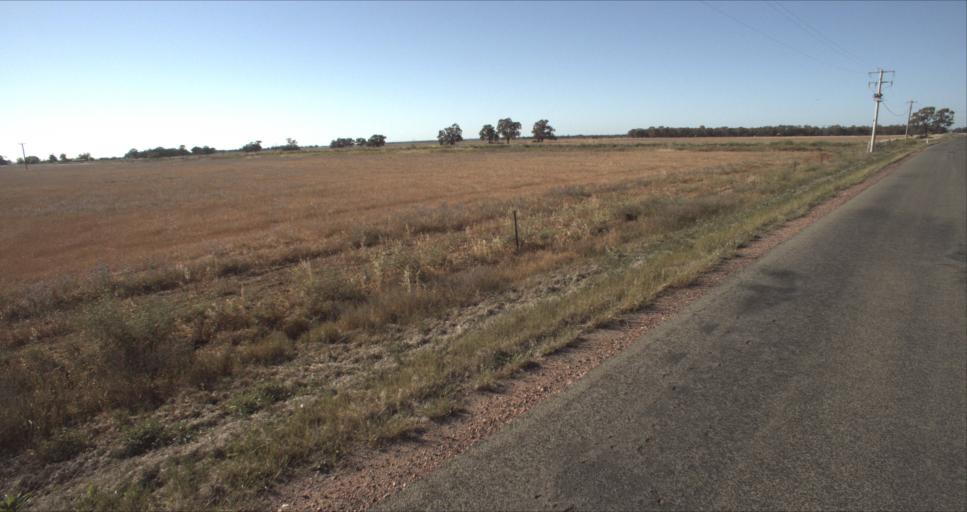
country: AU
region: New South Wales
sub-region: Leeton
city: Leeton
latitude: -34.5537
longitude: 146.2668
